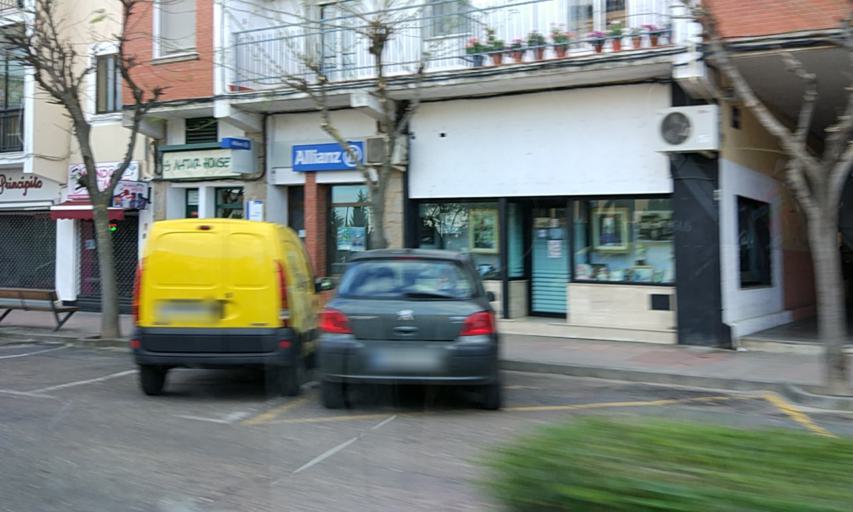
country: ES
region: Extremadura
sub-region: Provincia de Caceres
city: Coria
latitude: 39.9887
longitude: -6.5387
